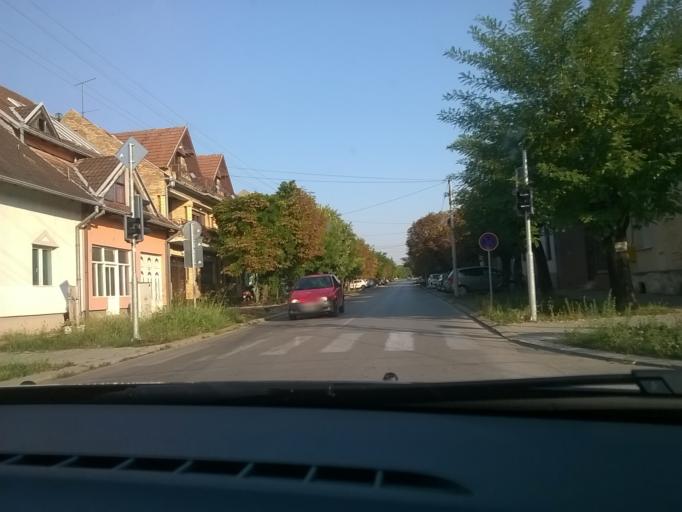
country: RS
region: Autonomna Pokrajina Vojvodina
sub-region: Juznobanatski Okrug
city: Vrsac
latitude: 45.1134
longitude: 21.3044
